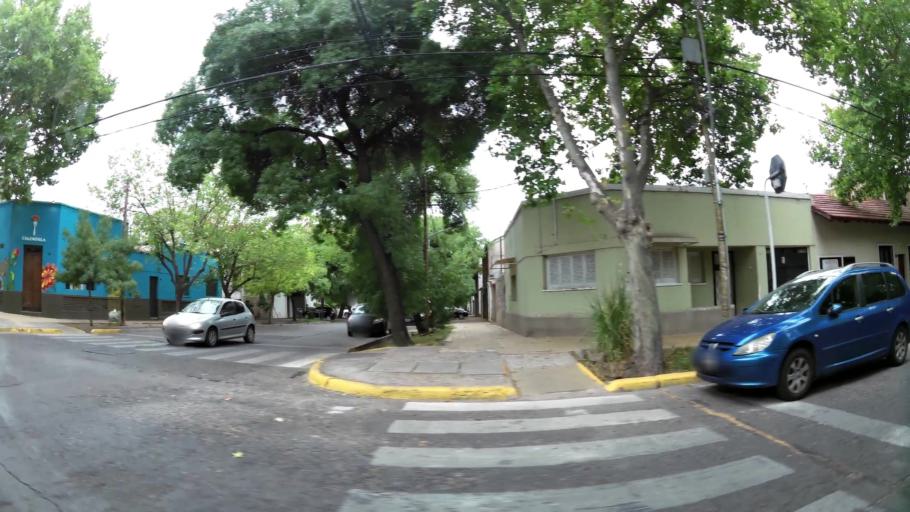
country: AR
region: Mendoza
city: Mendoza
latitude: -32.8830
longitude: -68.8518
